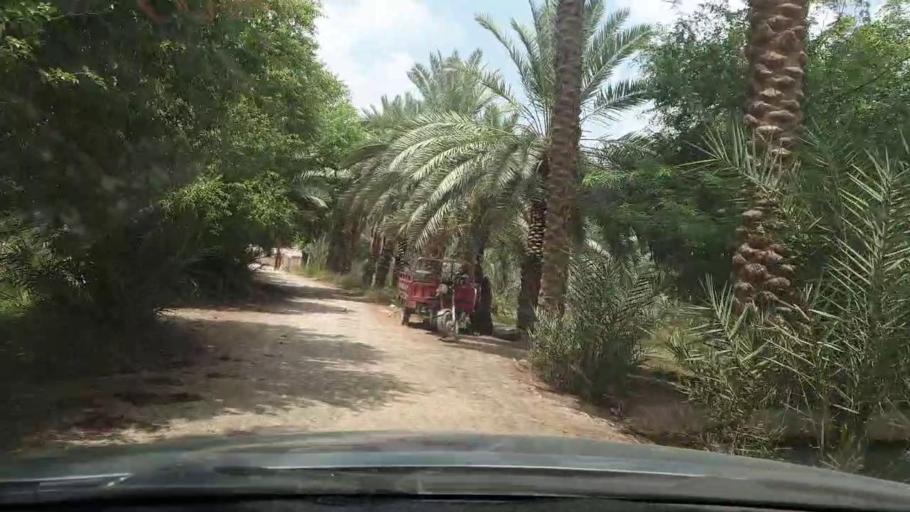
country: PK
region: Sindh
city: Kot Diji
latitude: 27.4265
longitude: 68.7687
